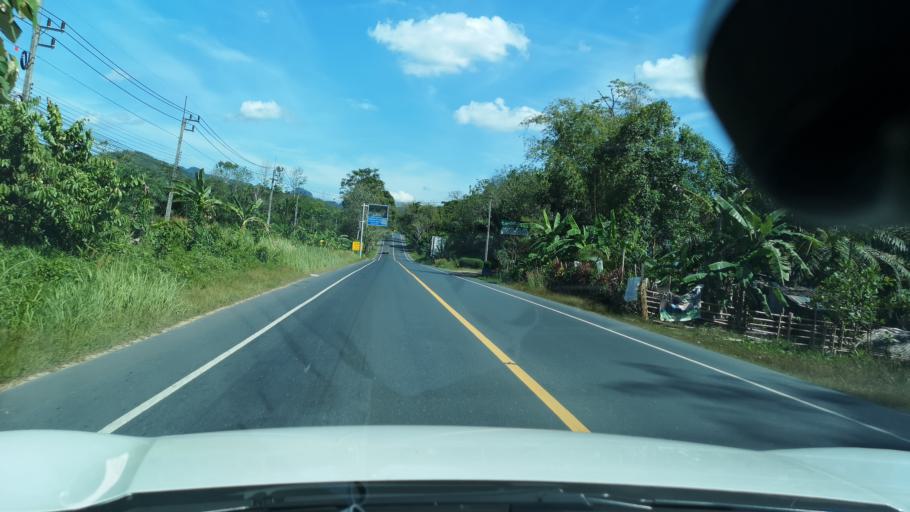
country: TH
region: Phangnga
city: Phang Nga
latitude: 8.5331
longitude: 98.5098
